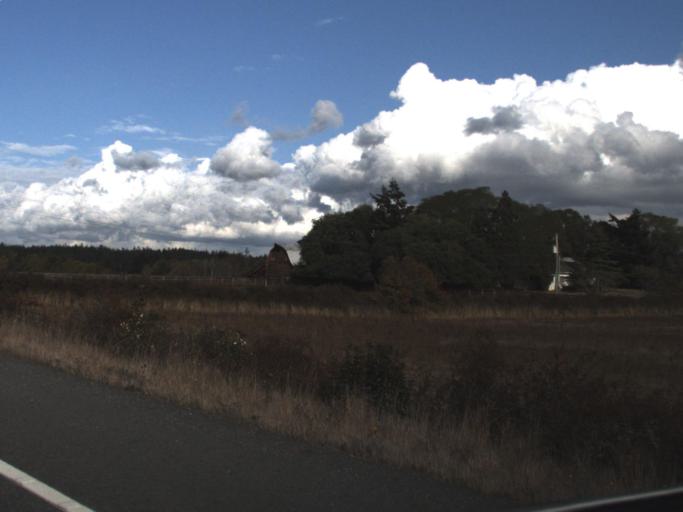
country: US
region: Washington
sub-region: Island County
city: Coupeville
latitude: 48.2414
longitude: -122.7141
